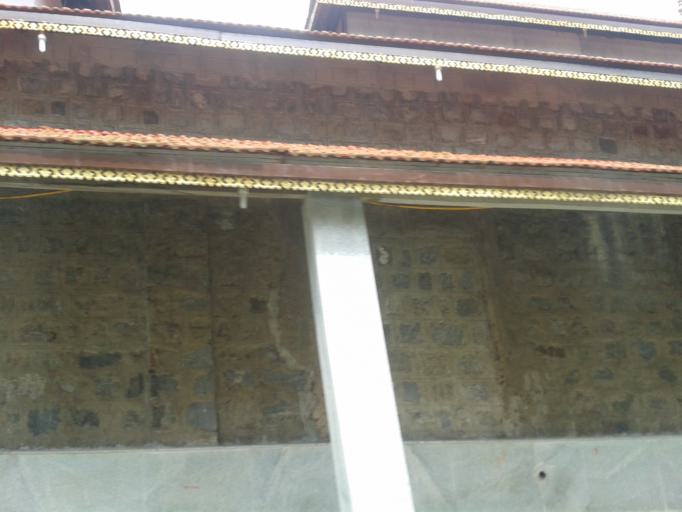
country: IN
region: Karnataka
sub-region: Chikmagalur
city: Mudigere
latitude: 13.0257
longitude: 75.6216
